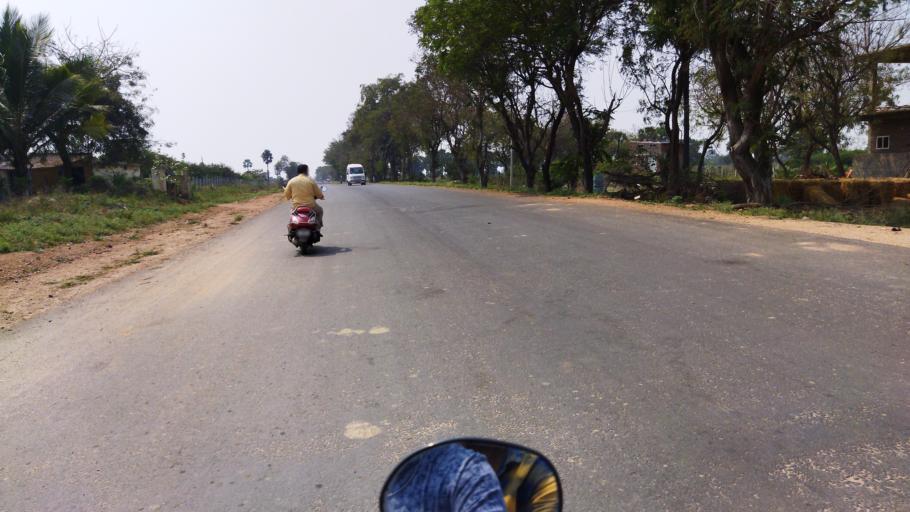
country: IN
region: Telangana
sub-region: Nalgonda
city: Nalgonda
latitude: 17.1589
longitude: 79.4180
